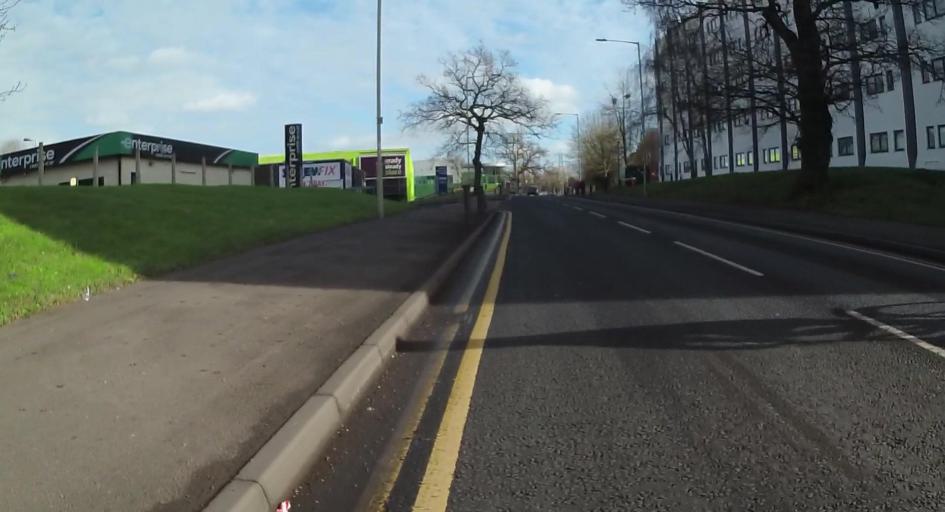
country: GB
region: England
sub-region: Wokingham
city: Wokingham
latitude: 51.4044
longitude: -0.8435
